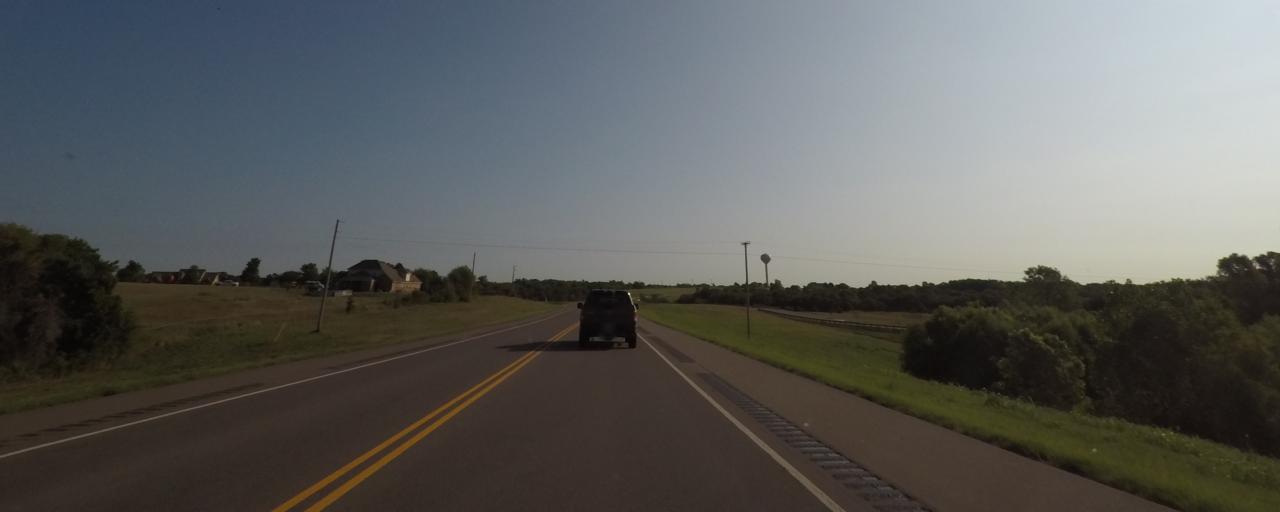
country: US
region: Oklahoma
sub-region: McClain County
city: Blanchard
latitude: 35.1178
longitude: -97.7074
